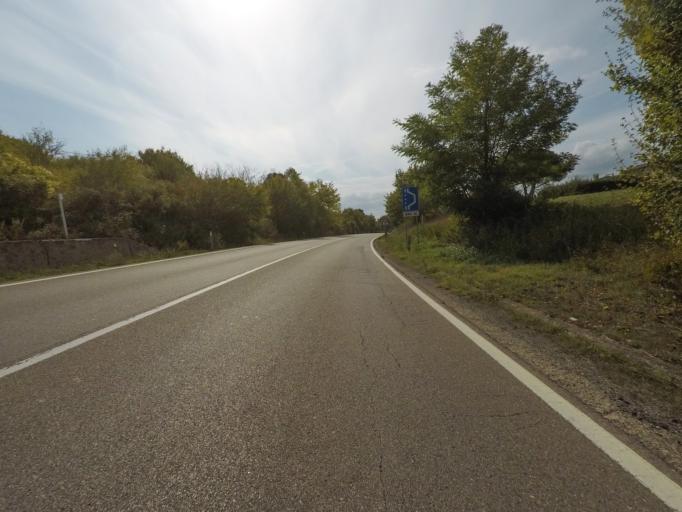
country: IT
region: Tuscany
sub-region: Provincia di Siena
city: Rosia
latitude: 43.2086
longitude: 11.2791
